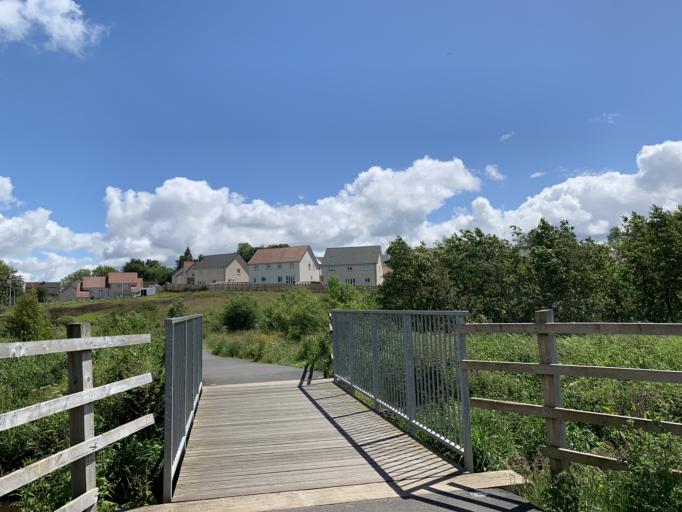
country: GB
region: Scotland
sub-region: East Renfrewshire
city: Newton Mearns
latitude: 55.7831
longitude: -4.3318
